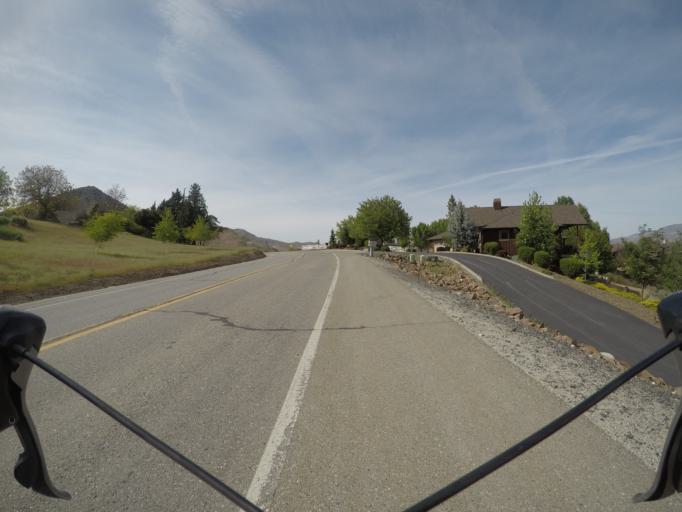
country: US
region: Washington
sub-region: Chelan County
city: West Wenatchee
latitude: 47.4113
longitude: -120.3425
